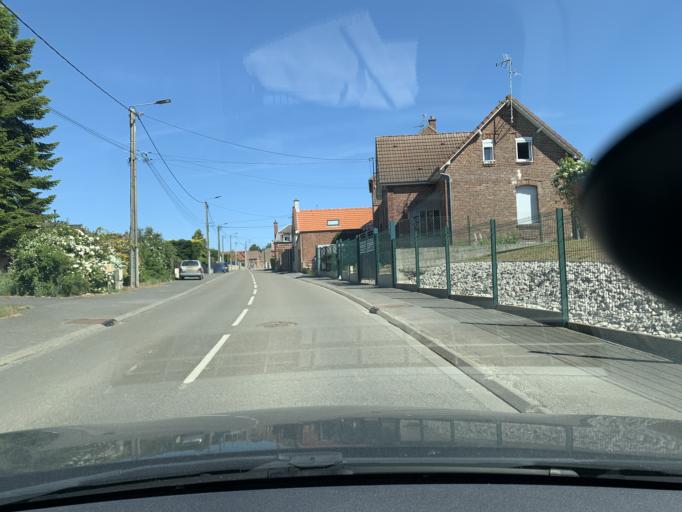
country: FR
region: Nord-Pas-de-Calais
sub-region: Departement du Nord
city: Fontaine-Notre-Dame
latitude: 50.1632
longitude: 3.1576
